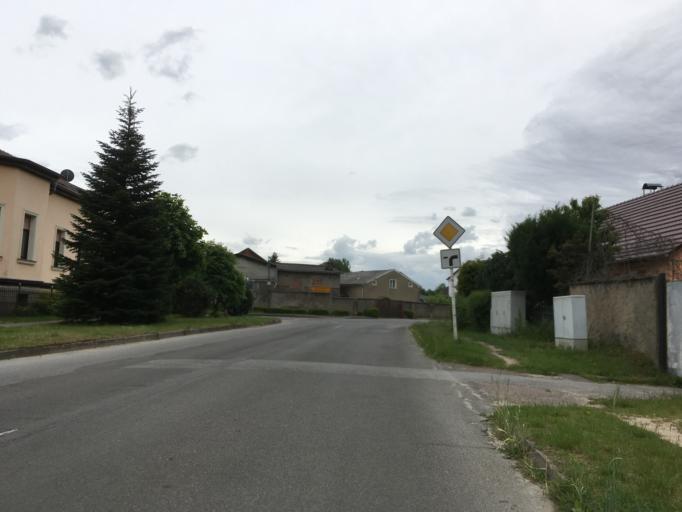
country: DE
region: Brandenburg
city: Werneuchen
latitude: 52.6641
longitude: 13.6884
